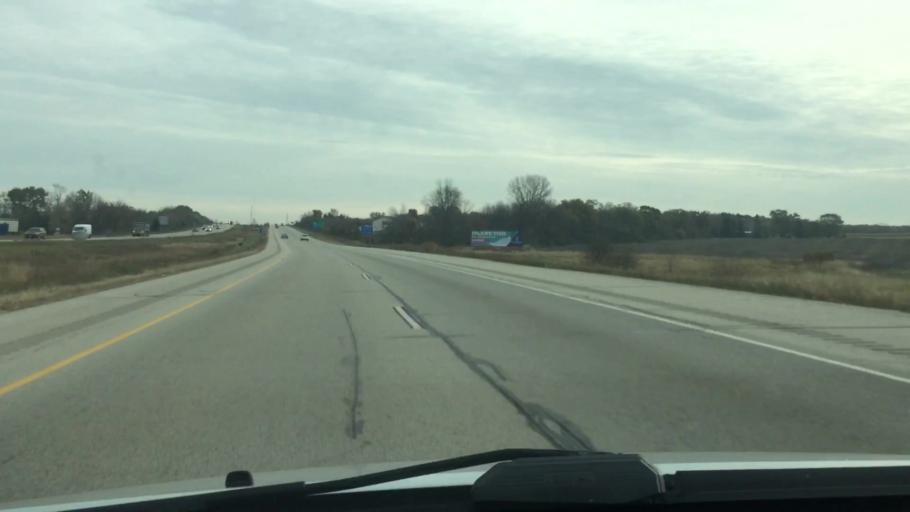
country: US
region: Wisconsin
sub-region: Waukesha County
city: Big Bend
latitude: 42.9144
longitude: -88.2068
